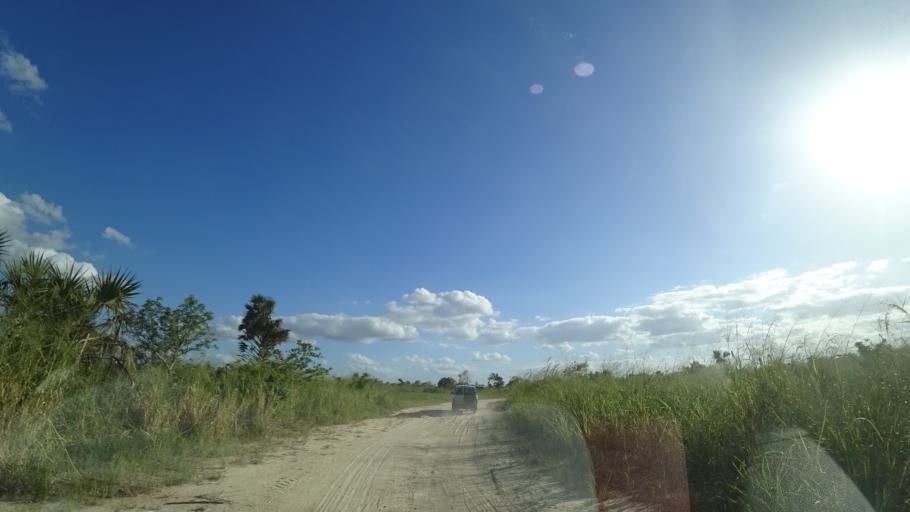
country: MZ
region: Sofala
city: Dondo
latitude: -19.3866
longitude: 34.5918
